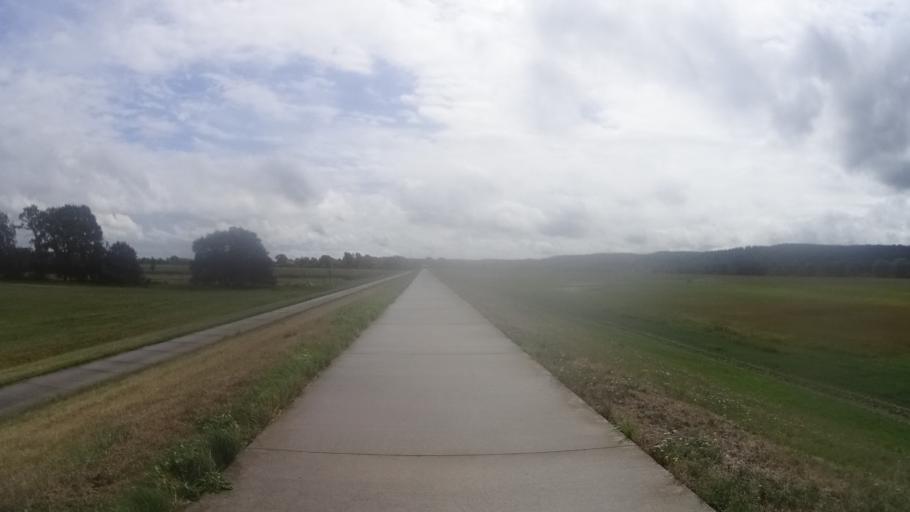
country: DE
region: Lower Saxony
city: Neu Darchau
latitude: 53.2309
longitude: 10.9287
